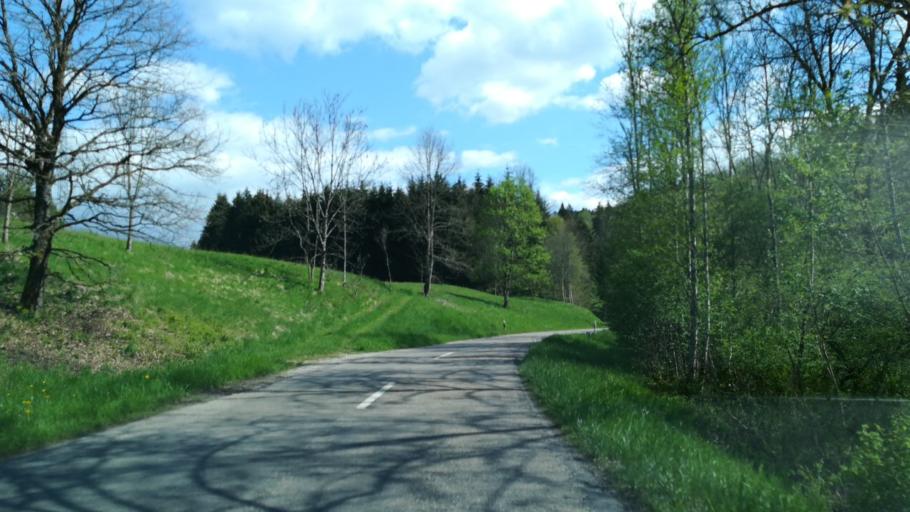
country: DE
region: Baden-Wuerttemberg
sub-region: Freiburg Region
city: Blumberg
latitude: 47.8472
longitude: 8.4594
